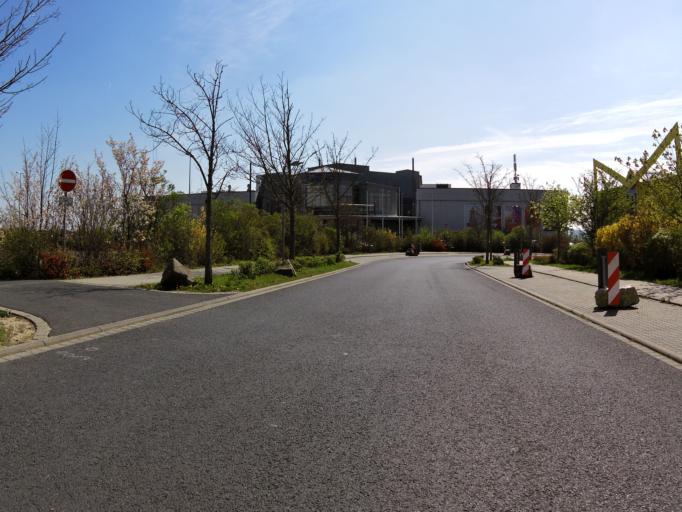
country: DE
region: Bavaria
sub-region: Regierungsbezirk Unterfranken
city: Biebelried
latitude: 49.7789
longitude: 10.0698
